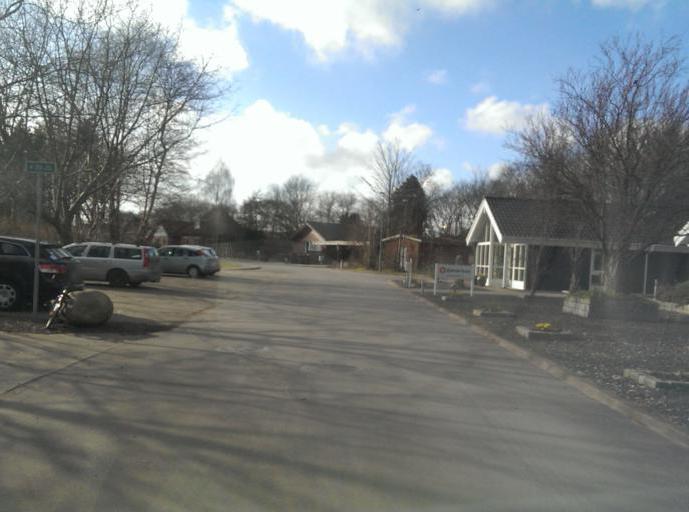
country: DK
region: South Denmark
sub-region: Esbjerg Kommune
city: Bramming
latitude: 55.4634
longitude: 8.7107
